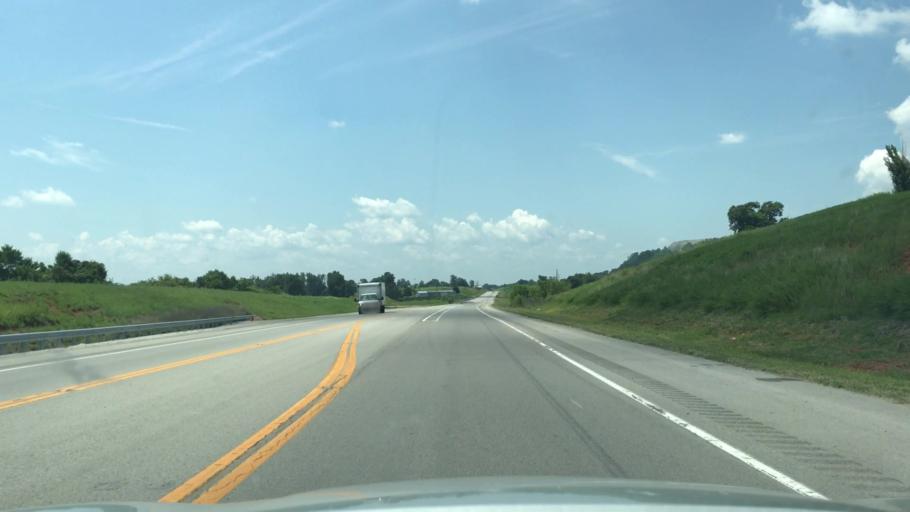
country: US
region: Kentucky
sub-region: Clinton County
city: Albany
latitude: 36.7189
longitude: -85.1412
